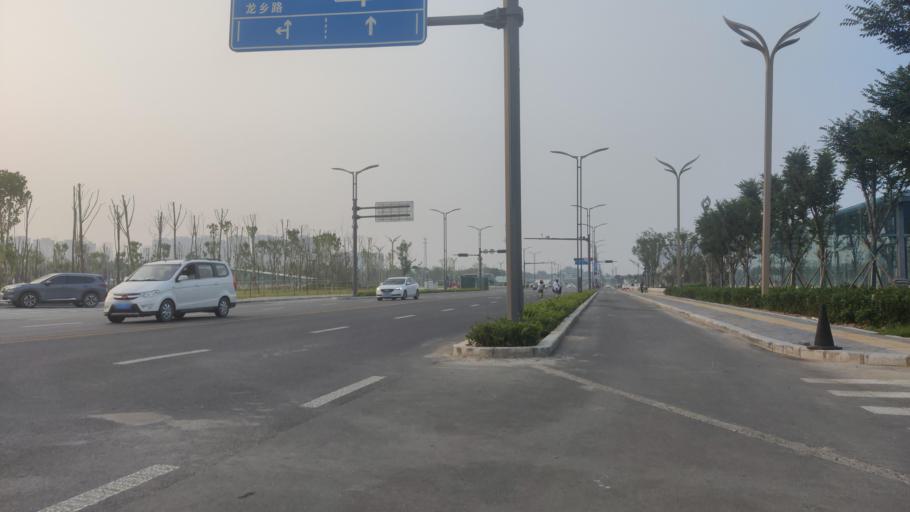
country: CN
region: Henan Sheng
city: Zhongyuanlu
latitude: 35.7633
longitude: 115.1413
